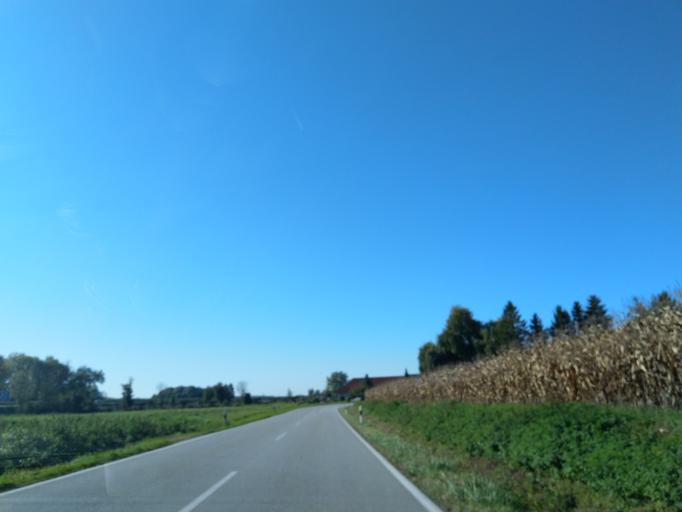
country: DE
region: Bavaria
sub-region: Lower Bavaria
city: Plattling
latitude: 48.8030
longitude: 12.9176
